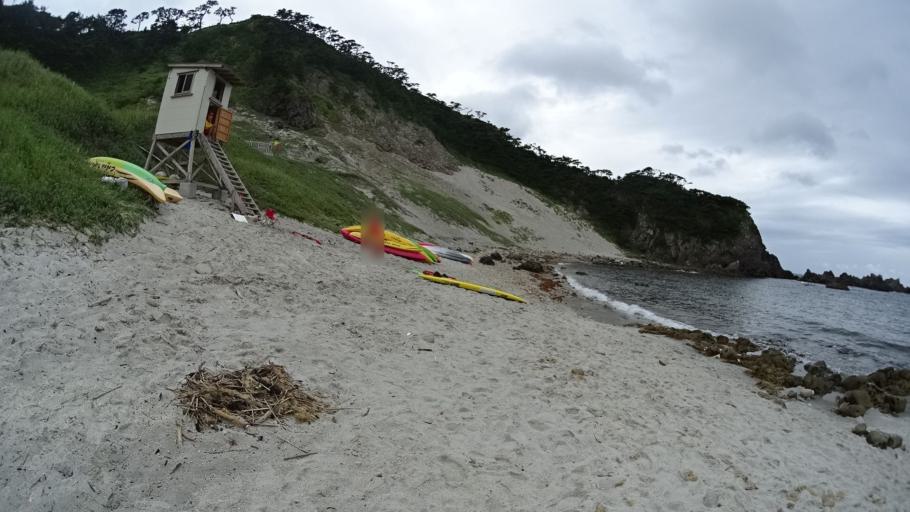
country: JP
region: Shizuoka
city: Shimoda
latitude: 34.3300
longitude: 139.2084
